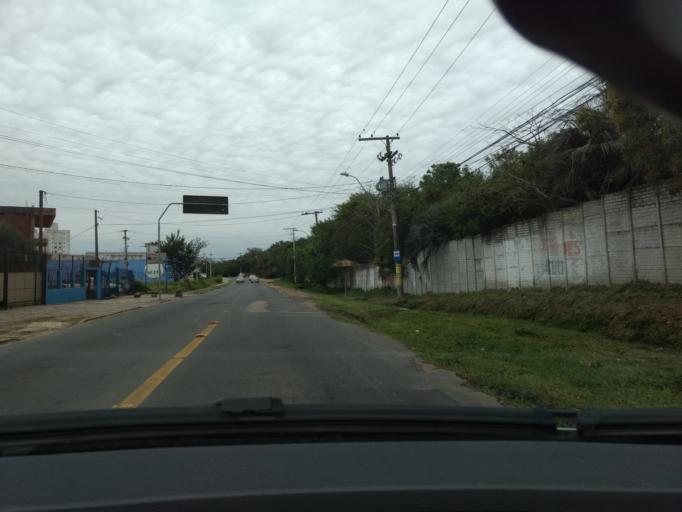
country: BR
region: Rio Grande do Sul
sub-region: Cachoeirinha
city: Cachoeirinha
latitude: -30.0313
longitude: -51.1342
